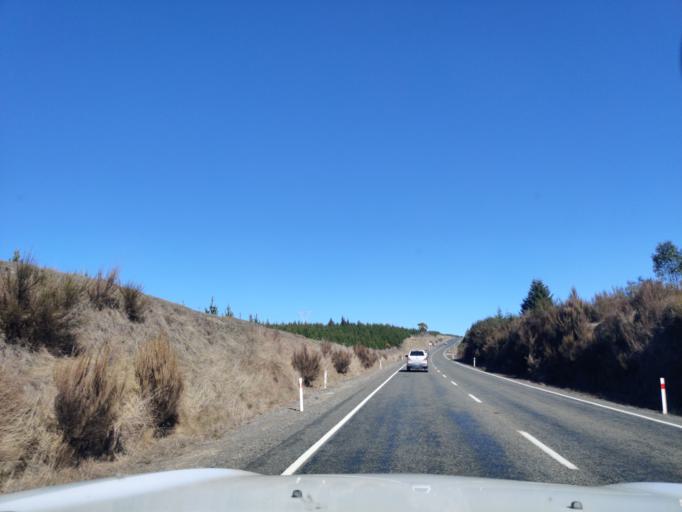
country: NZ
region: Waikato
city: Turangi
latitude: -39.1113
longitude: 175.8059
